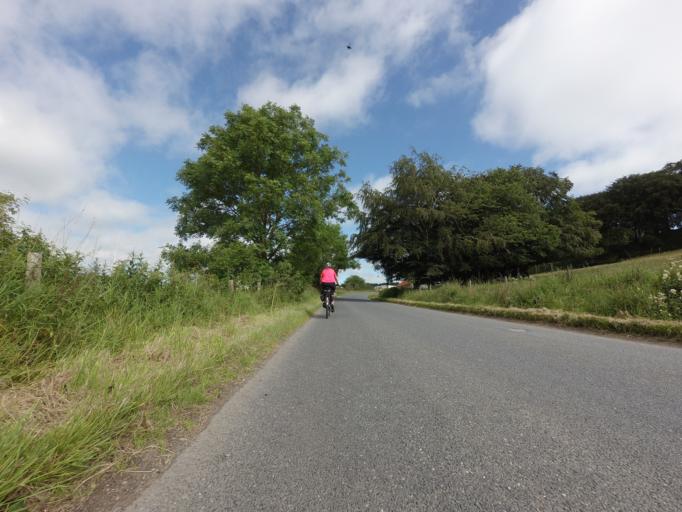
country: GB
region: Scotland
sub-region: Aberdeenshire
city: Turriff
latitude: 57.5627
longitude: -2.4940
